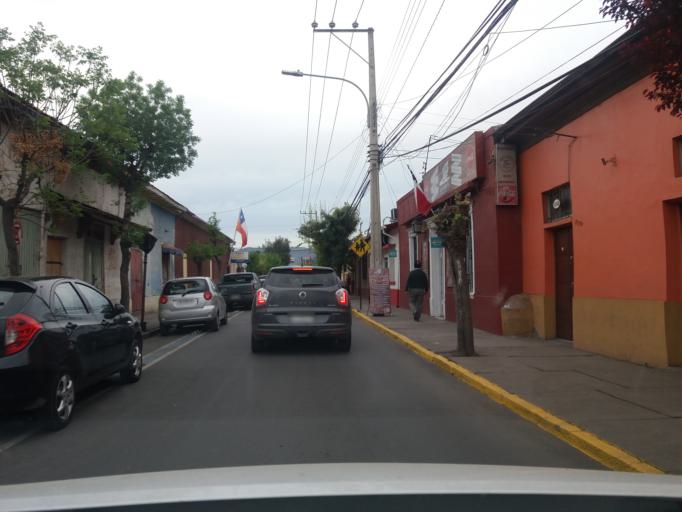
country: CL
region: Valparaiso
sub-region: Provincia de San Felipe
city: San Felipe
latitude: -32.7544
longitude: -70.7257
